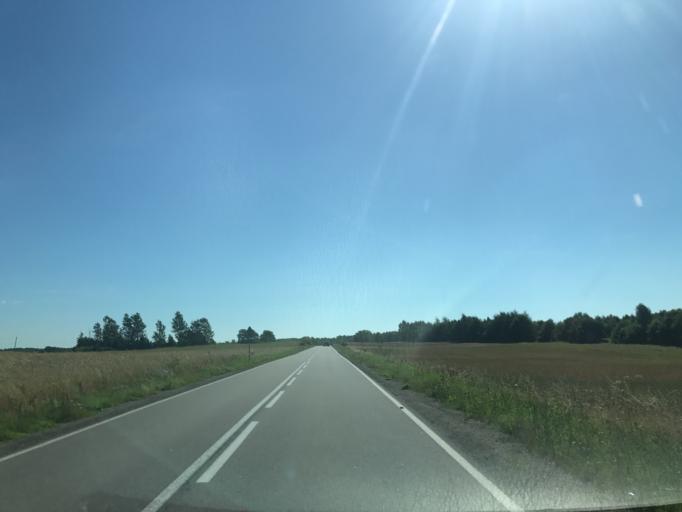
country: PL
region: Pomeranian Voivodeship
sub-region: Powiat leborski
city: Cewice
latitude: 54.3389
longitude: 17.6948
